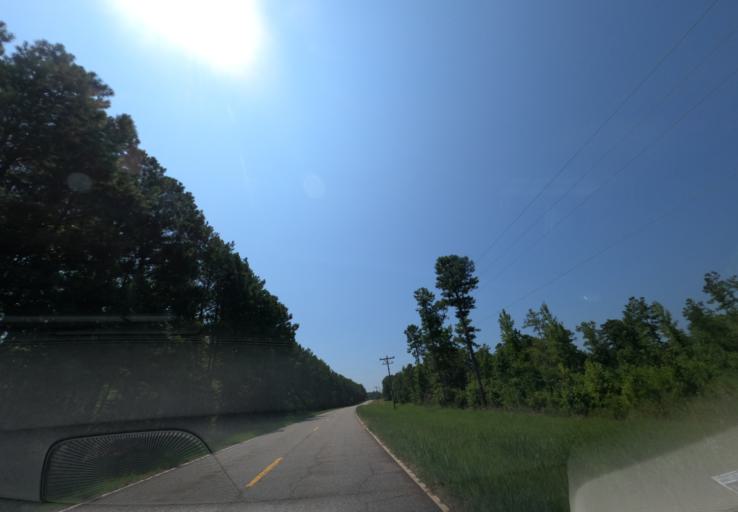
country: US
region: South Carolina
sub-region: Greenwood County
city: Greenwood
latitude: 34.0415
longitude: -82.1308
